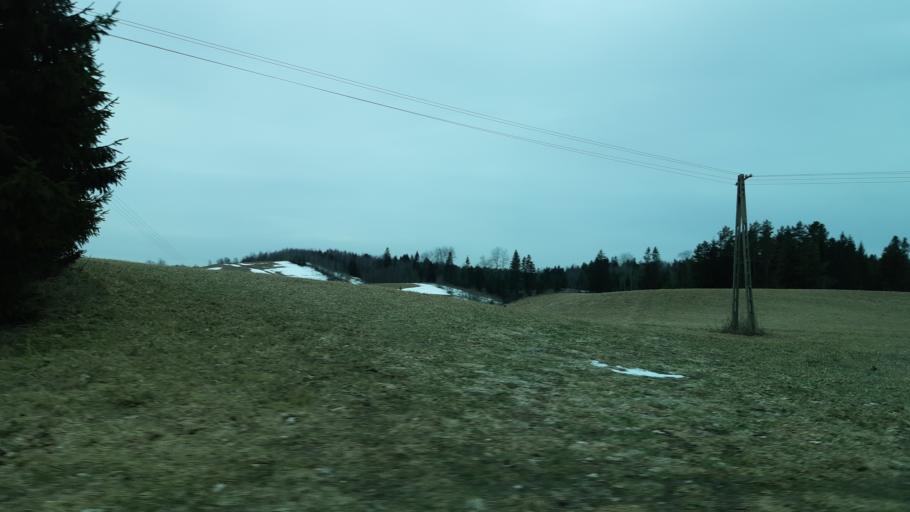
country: LT
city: Virbalis
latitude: 54.3778
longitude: 22.8201
